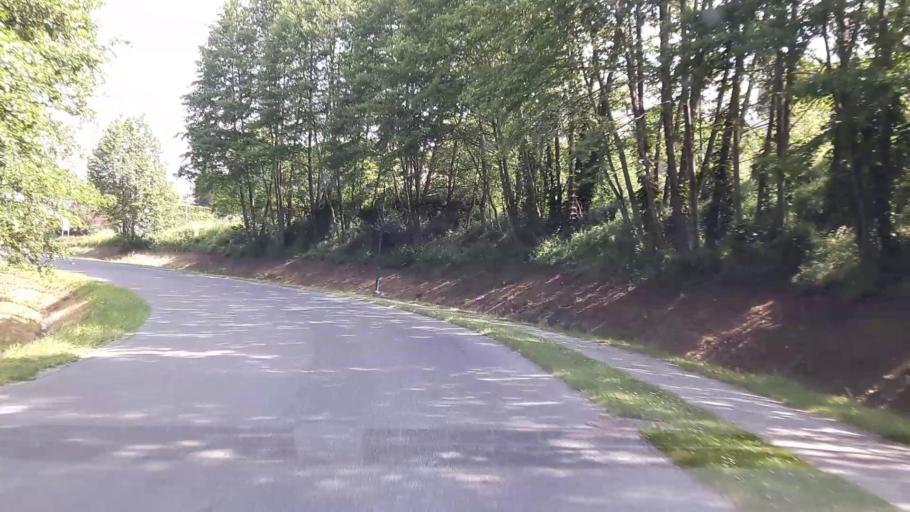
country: AT
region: Burgenland
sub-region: Politischer Bezirk Gussing
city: Stegersbach
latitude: 47.1688
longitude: 16.1492
